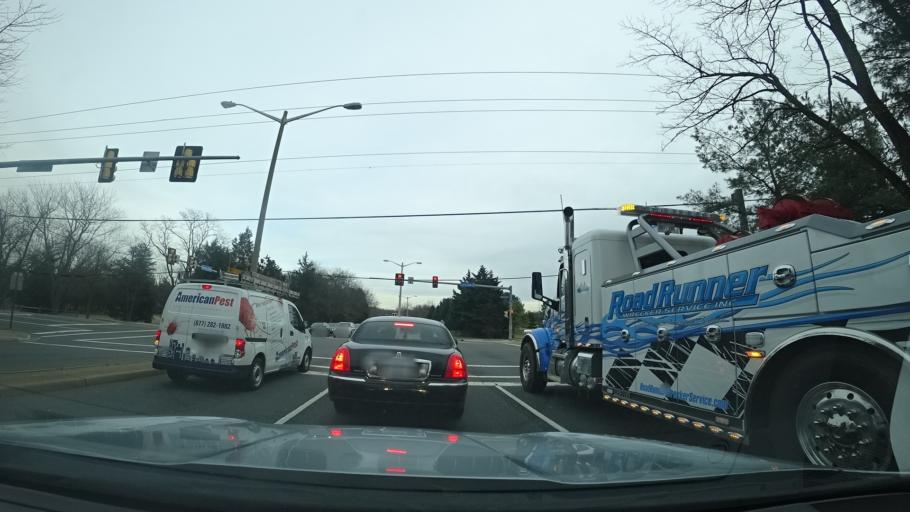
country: US
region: Virginia
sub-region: Loudoun County
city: Oak Grove
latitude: 38.9778
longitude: -77.3994
